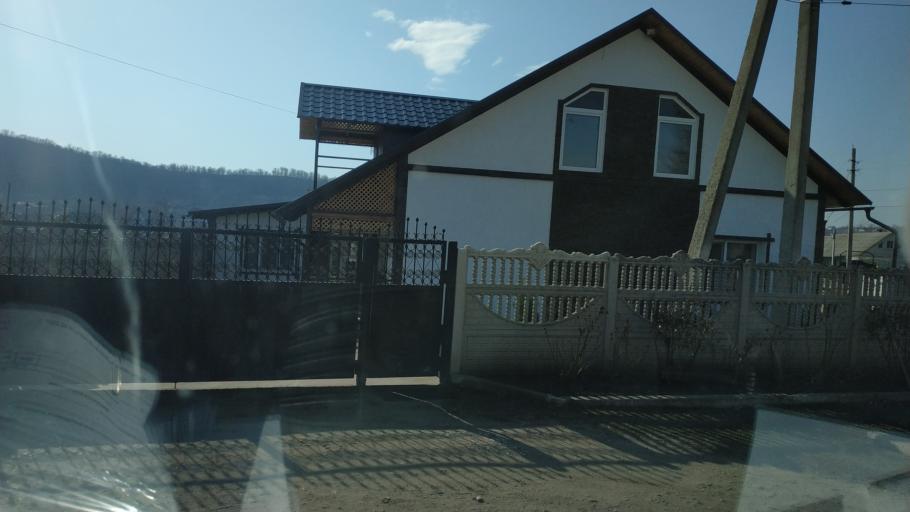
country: MD
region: Chisinau
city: Singera
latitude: 46.6821
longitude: 29.0518
